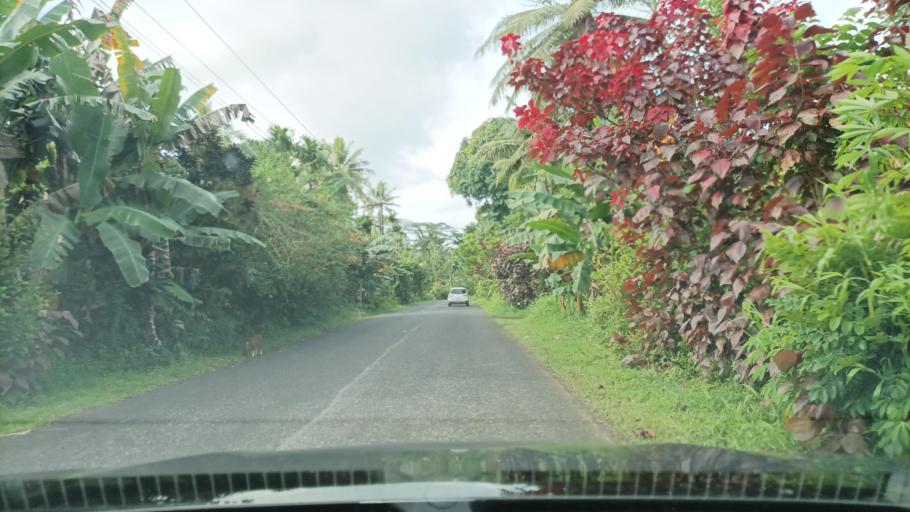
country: FM
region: Pohnpei
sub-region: Sokehs Municipality
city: Palikir - National Government Center
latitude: 6.9157
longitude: 158.1598
